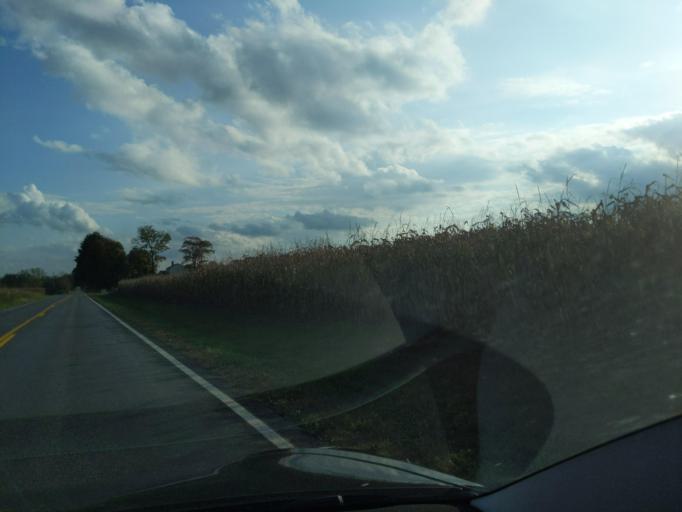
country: US
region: Michigan
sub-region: Ingham County
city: Leslie
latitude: 42.3473
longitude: -84.4629
